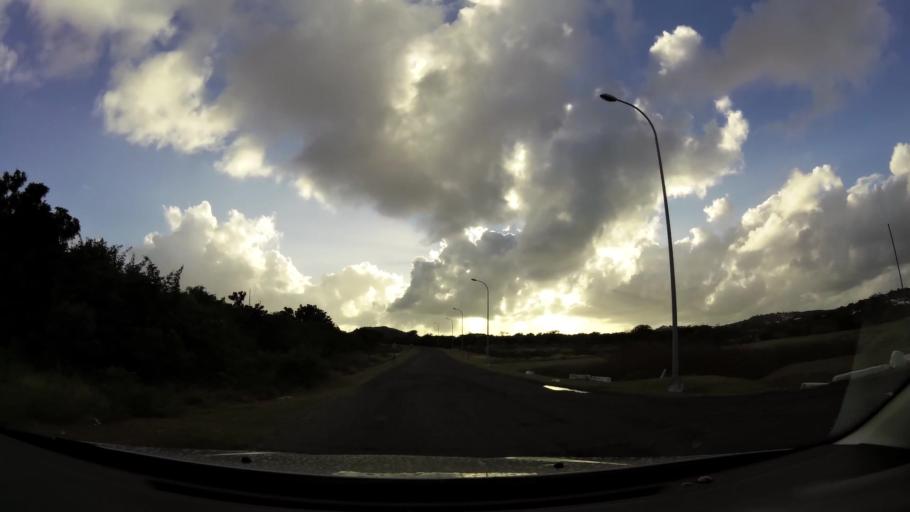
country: AG
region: Saint John
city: Saint John's
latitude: 17.1576
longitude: -61.8269
